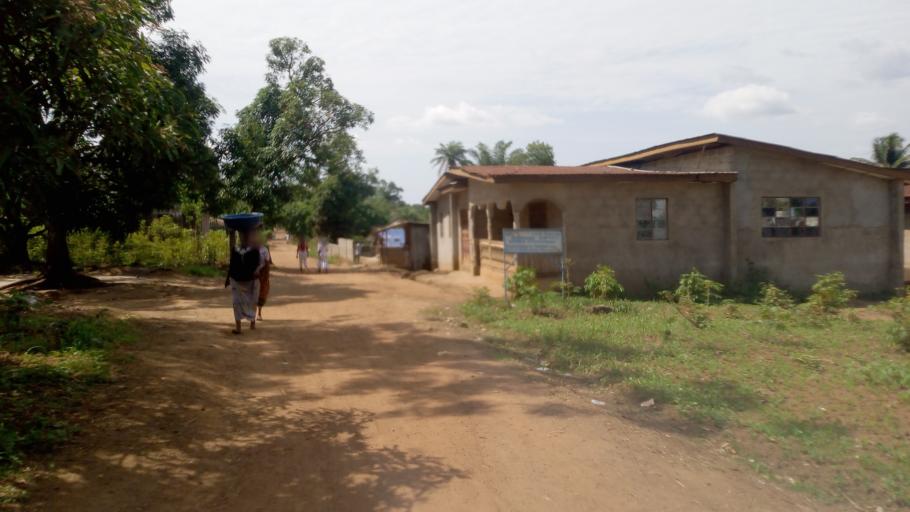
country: SL
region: Western Area
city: Waterloo
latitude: 8.3185
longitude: -13.0720
